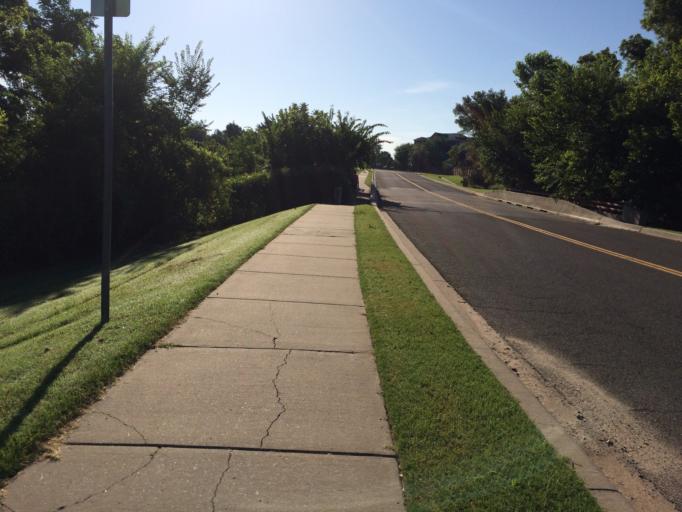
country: US
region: Oklahoma
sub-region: Cleveland County
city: Norman
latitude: 35.1917
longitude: -97.4285
